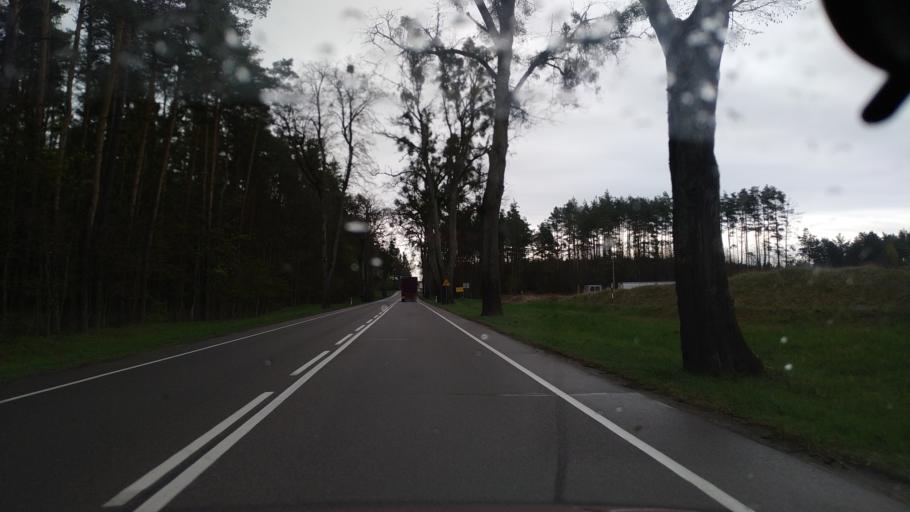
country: PL
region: Pomeranian Voivodeship
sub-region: Powiat starogardzki
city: Kaliska
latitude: 53.8827
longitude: 18.1938
